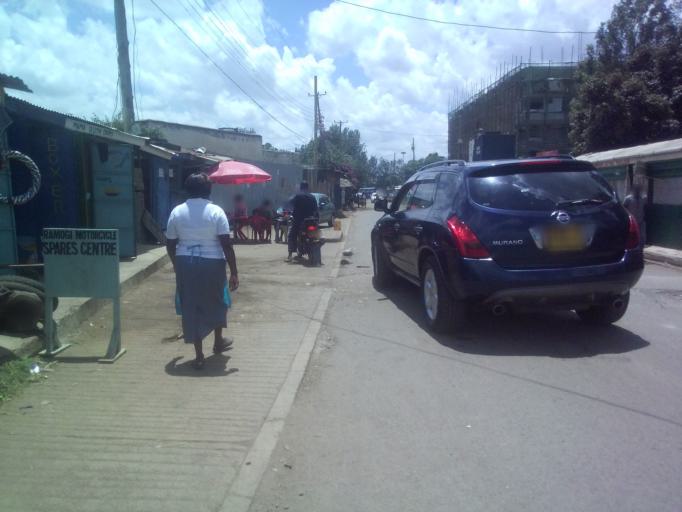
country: KE
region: Nairobi Area
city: Nairobi
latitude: -1.3097
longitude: 36.7784
